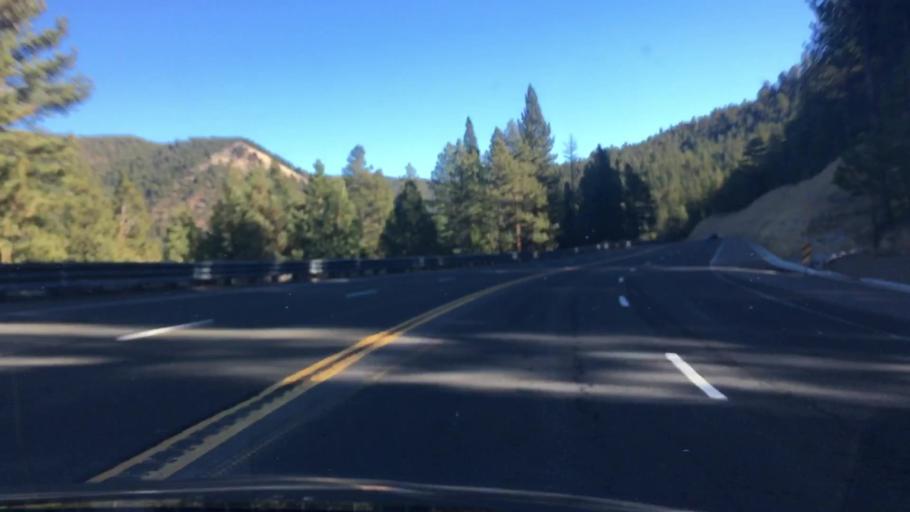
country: US
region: Nevada
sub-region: Douglas County
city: Kingsbury
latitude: 39.0825
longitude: -119.9403
